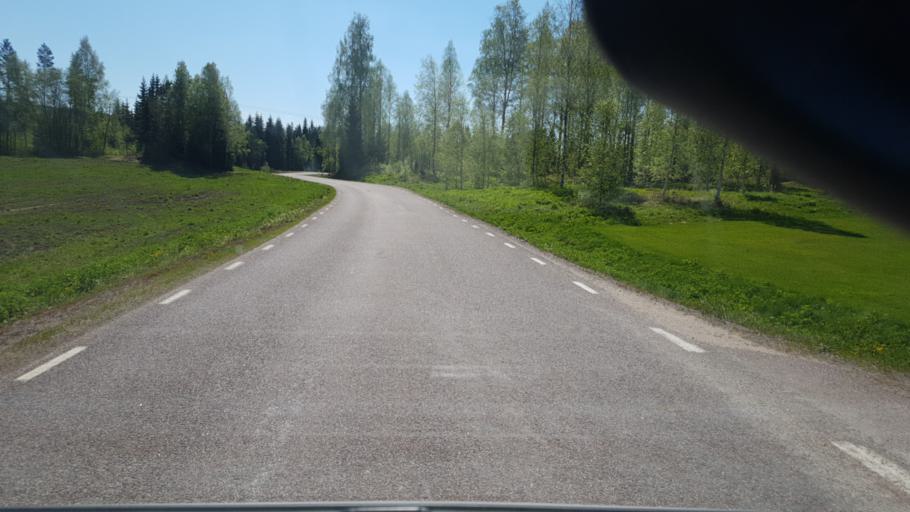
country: SE
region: Vaermland
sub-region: Arvika Kommun
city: Arvika
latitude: 59.7588
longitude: 12.8229
